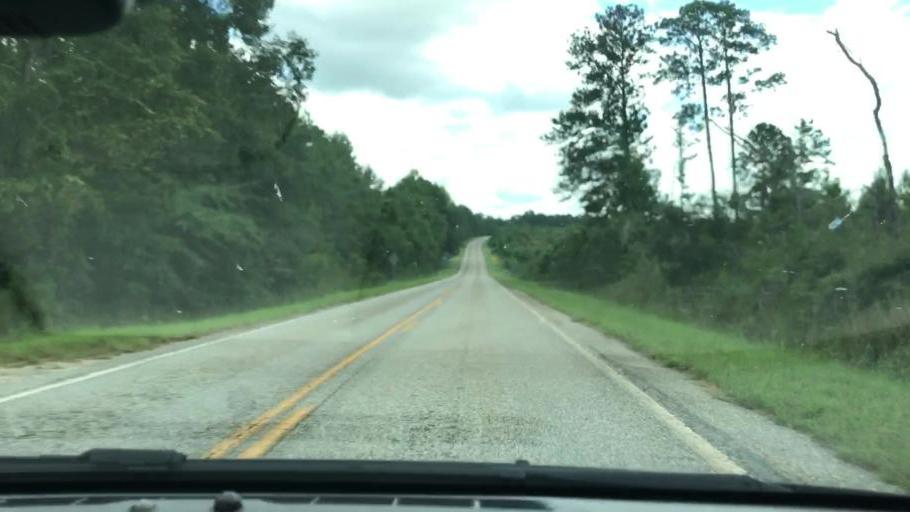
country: US
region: Georgia
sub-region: Stewart County
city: Lumpkin
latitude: 32.0724
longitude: -84.8503
